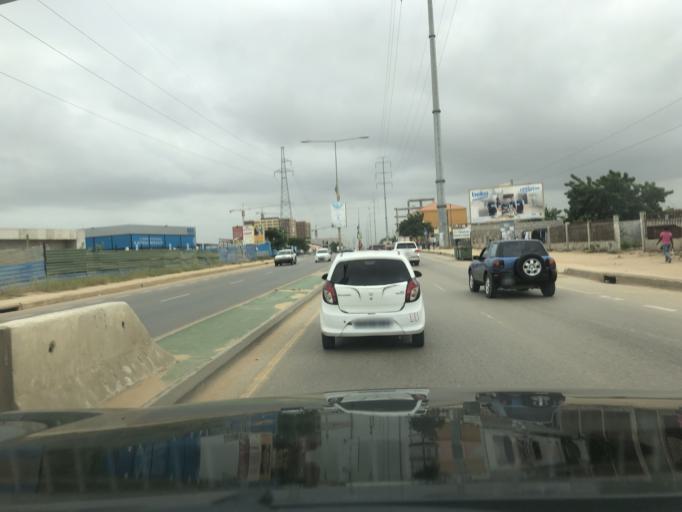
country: AO
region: Luanda
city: Luanda
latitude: -8.9736
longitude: 13.2098
